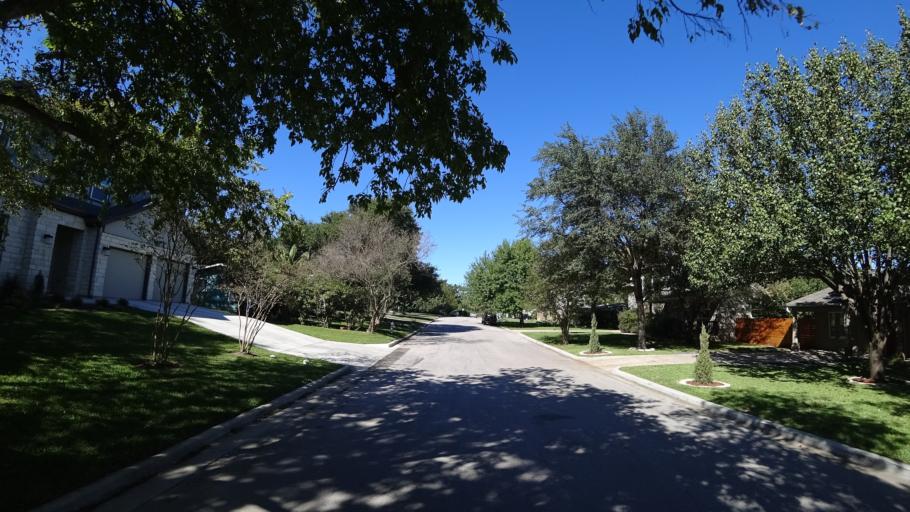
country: US
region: Texas
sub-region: Travis County
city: West Lake Hills
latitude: 30.3282
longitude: -97.7531
